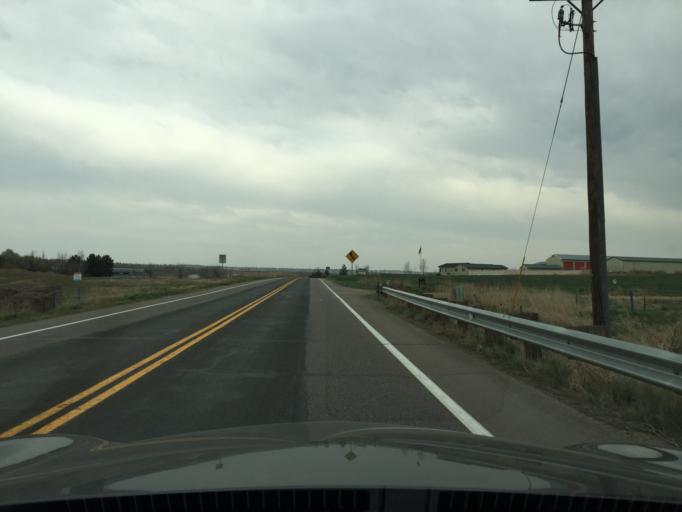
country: US
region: Colorado
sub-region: Boulder County
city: Lafayette
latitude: 40.0116
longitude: -105.0555
